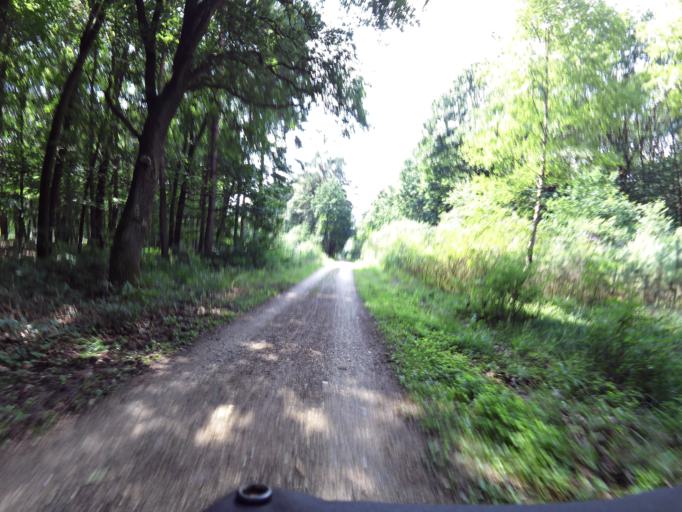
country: DE
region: North Rhine-Westphalia
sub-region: Regierungsbezirk Dusseldorf
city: Niederkruchten
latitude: 51.1674
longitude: 6.1854
